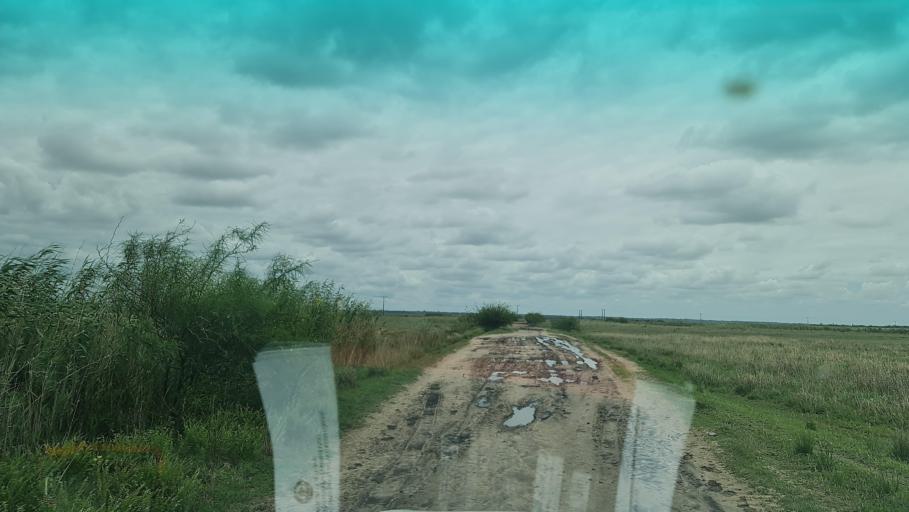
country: MZ
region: Maputo City
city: Maputo
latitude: -25.7263
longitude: 32.7016
